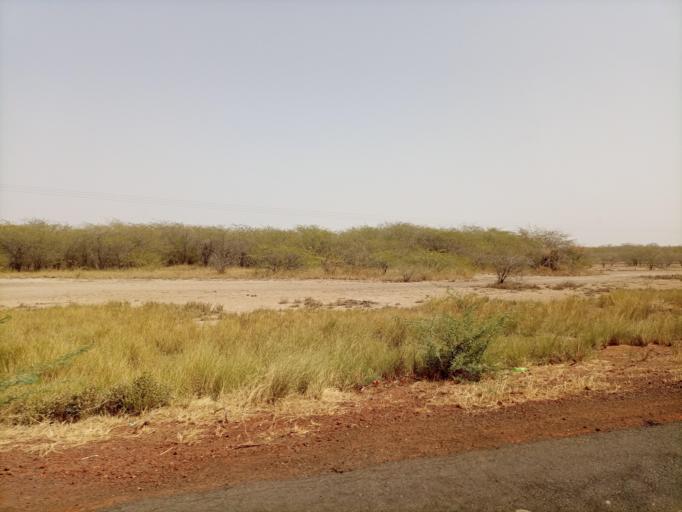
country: SN
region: Fatick
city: Foundiougne
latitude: 14.1800
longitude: -16.4573
